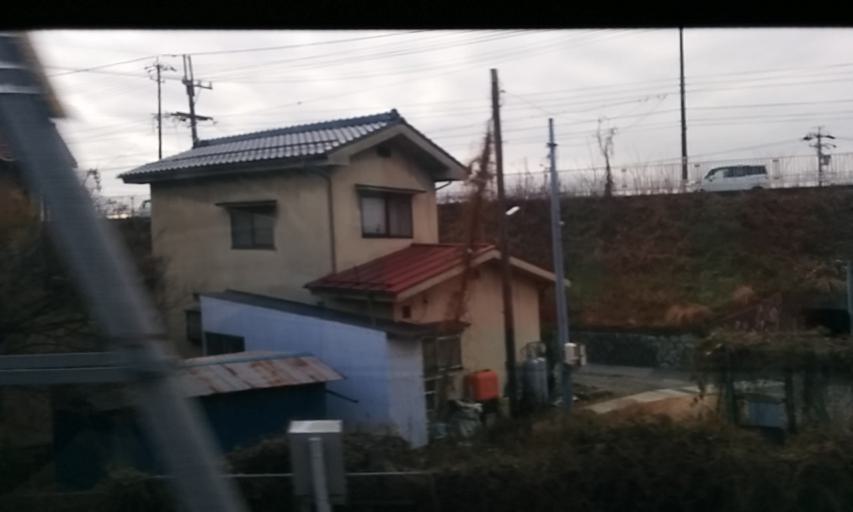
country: JP
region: Nagano
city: Matsumoto
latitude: 36.2419
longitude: 137.9548
